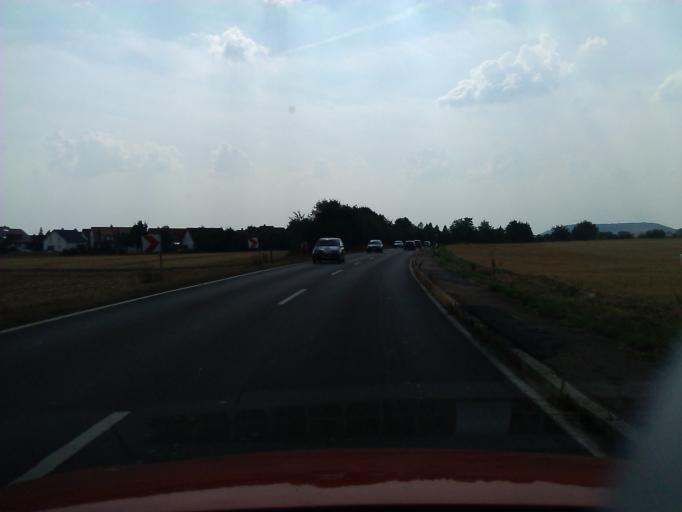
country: DE
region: Baden-Wuerttemberg
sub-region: Regierungsbezirk Stuttgart
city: Nordheim
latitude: 49.1131
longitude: 9.1459
